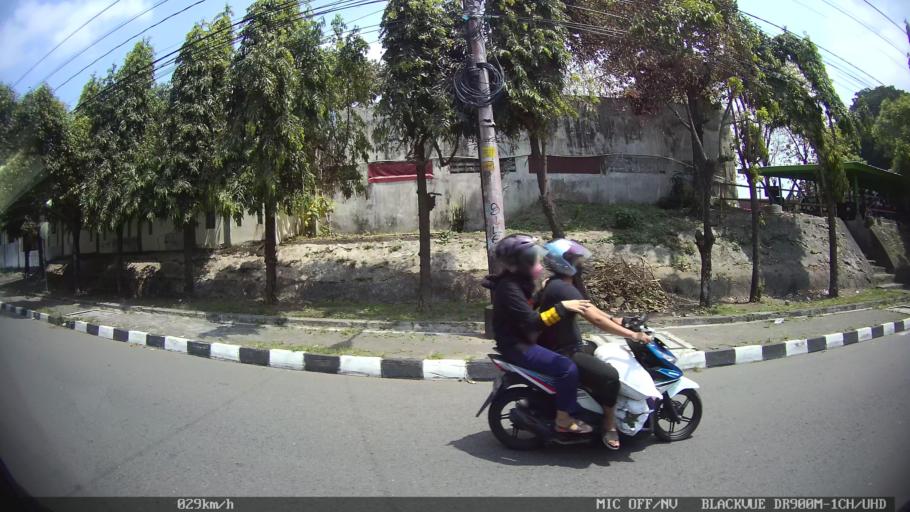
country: ID
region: Daerah Istimewa Yogyakarta
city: Yogyakarta
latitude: -7.8031
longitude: 110.3984
